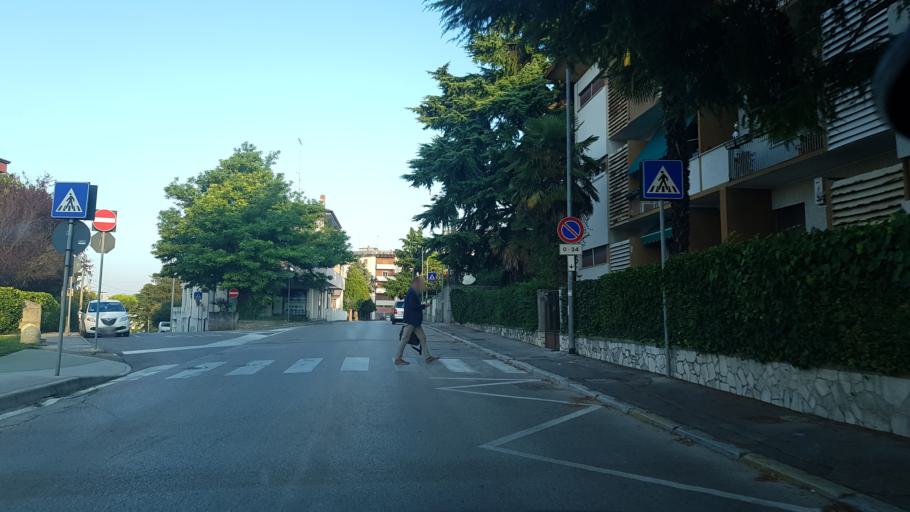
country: IT
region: Friuli Venezia Giulia
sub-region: Provincia di Gorizia
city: Monfalcone
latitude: 45.8059
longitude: 13.5435
